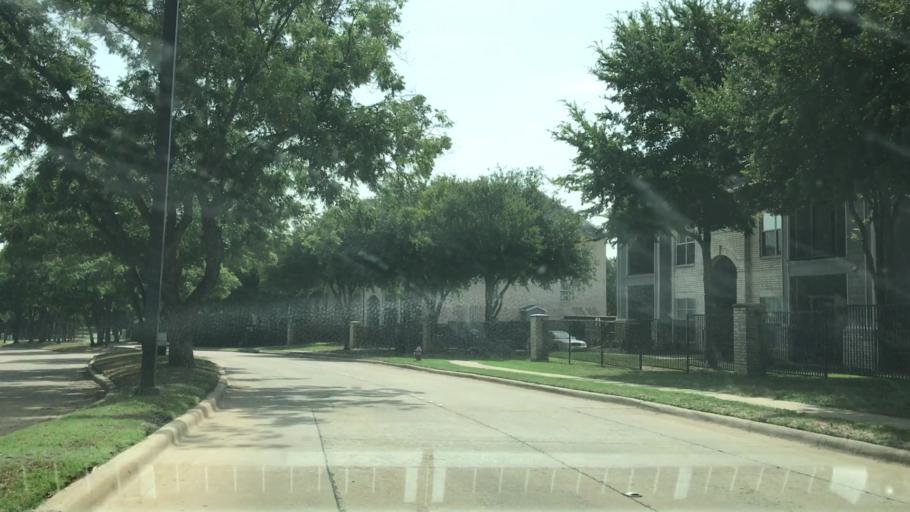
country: US
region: Texas
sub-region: Tarrant County
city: Euless
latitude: 32.8589
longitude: -97.0726
